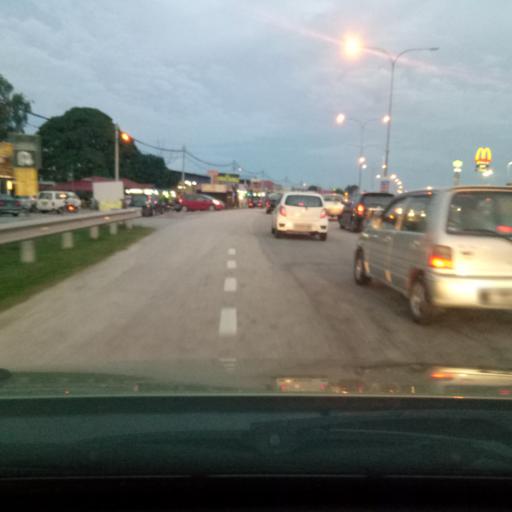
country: MY
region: Kedah
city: Alor Setar
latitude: 6.0974
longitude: 100.3745
